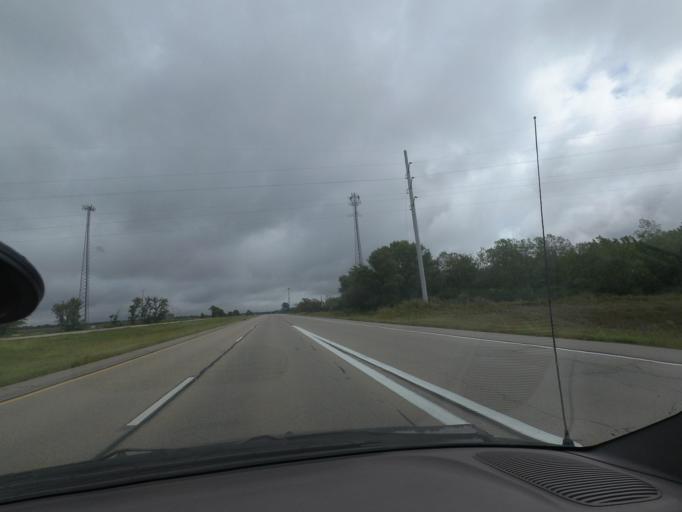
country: US
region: Illinois
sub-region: Piatt County
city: Monticello
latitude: 40.0379
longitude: -88.5928
